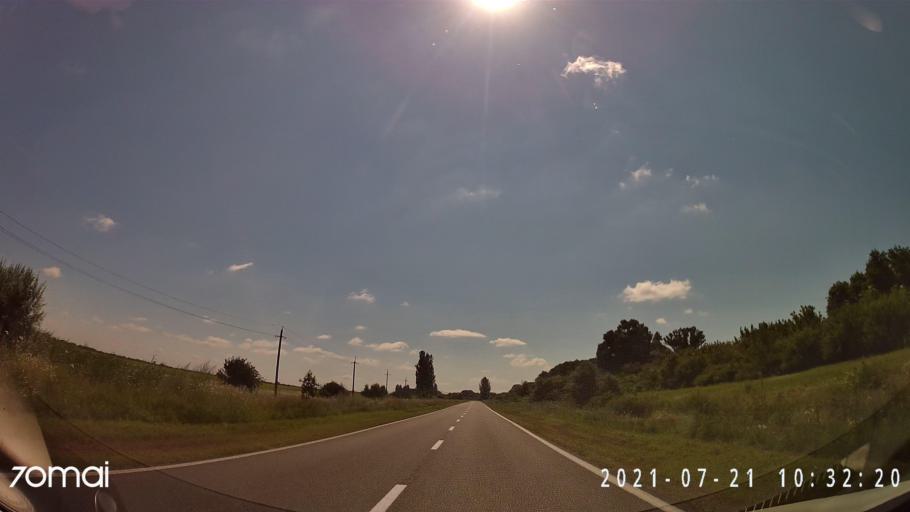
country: RO
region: Tulcea
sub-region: Oras Isaccea
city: Isaccea
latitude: 45.3024
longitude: 28.4210
